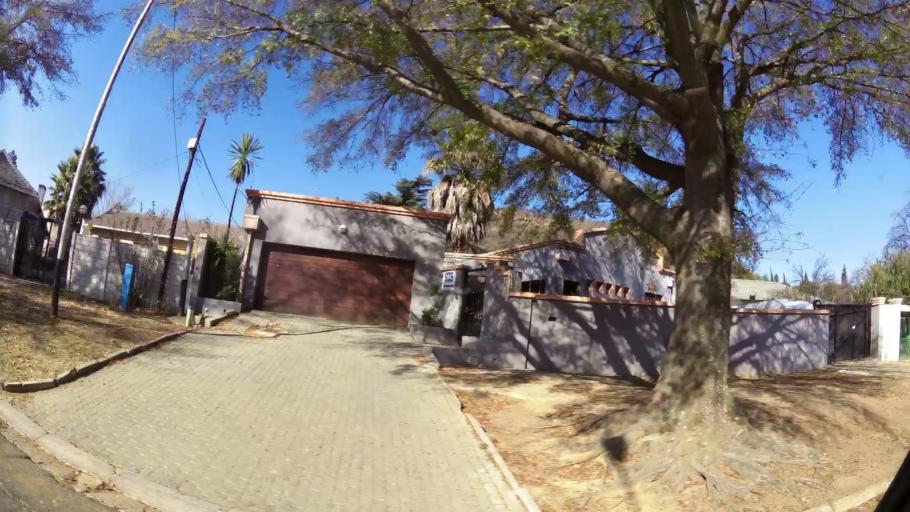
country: ZA
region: Gauteng
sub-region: City of Johannesburg Metropolitan Municipality
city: Johannesburg
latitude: -26.2798
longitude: 28.0098
